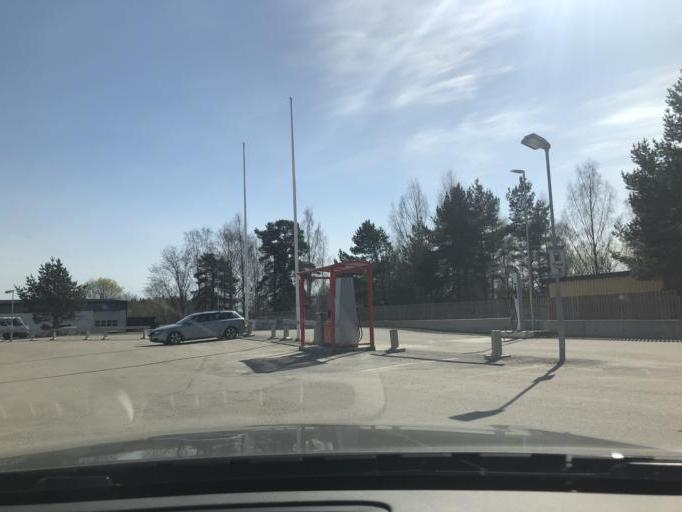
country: SE
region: Gaevleborg
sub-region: Hudiksvalls Kommun
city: Hudiksvall
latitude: 61.7239
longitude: 17.1452
